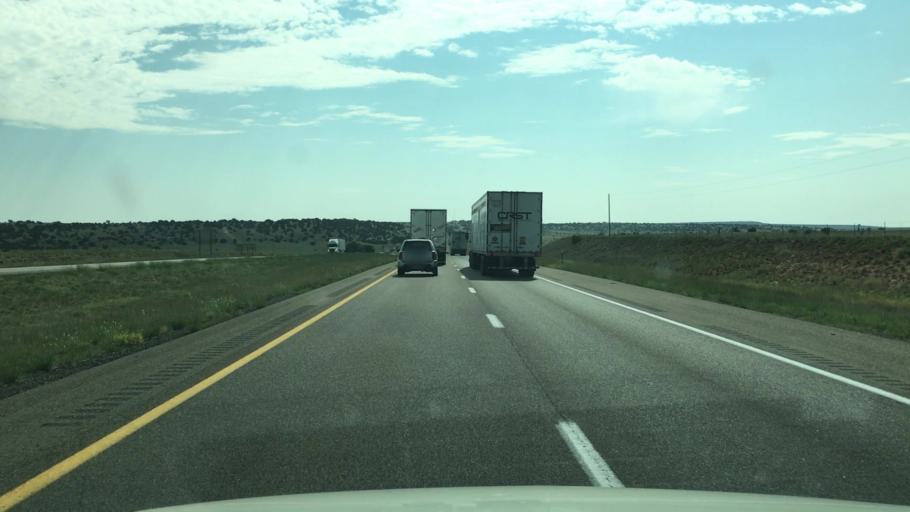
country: US
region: New Mexico
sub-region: Guadalupe County
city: Santa Rosa
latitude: 34.9758
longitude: -104.9799
